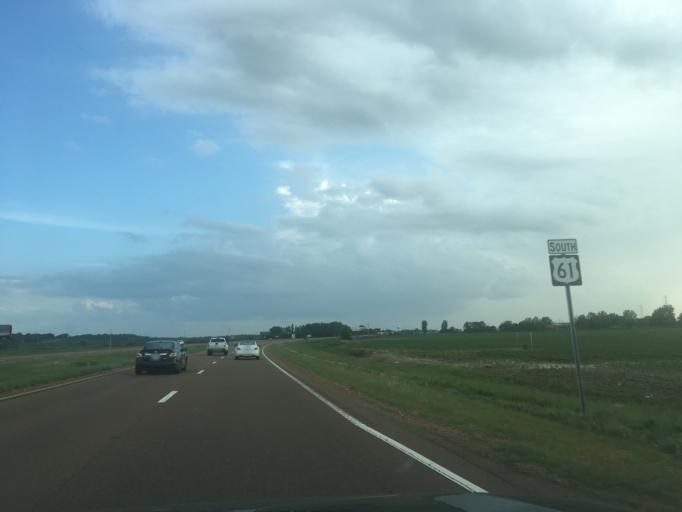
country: US
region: Mississippi
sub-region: De Soto County
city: Walls
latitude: 34.9557
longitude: -90.1425
